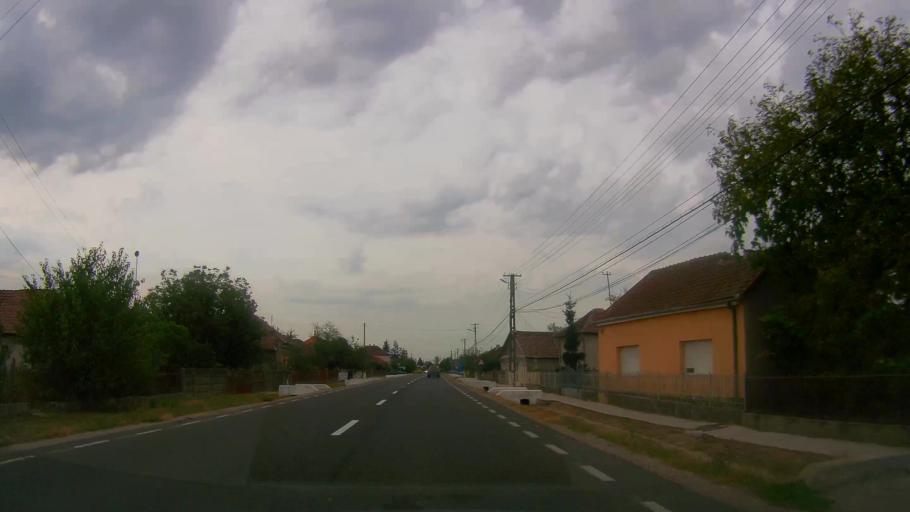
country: RO
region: Satu Mare
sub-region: Comuna Acas
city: Acas
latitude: 47.5313
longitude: 22.7828
